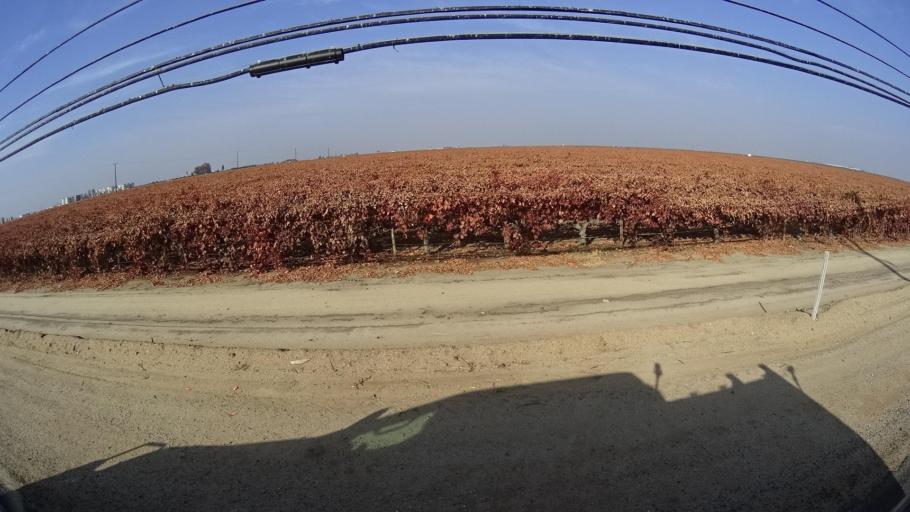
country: US
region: California
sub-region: Kern County
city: Delano
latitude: 35.7759
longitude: -119.1819
